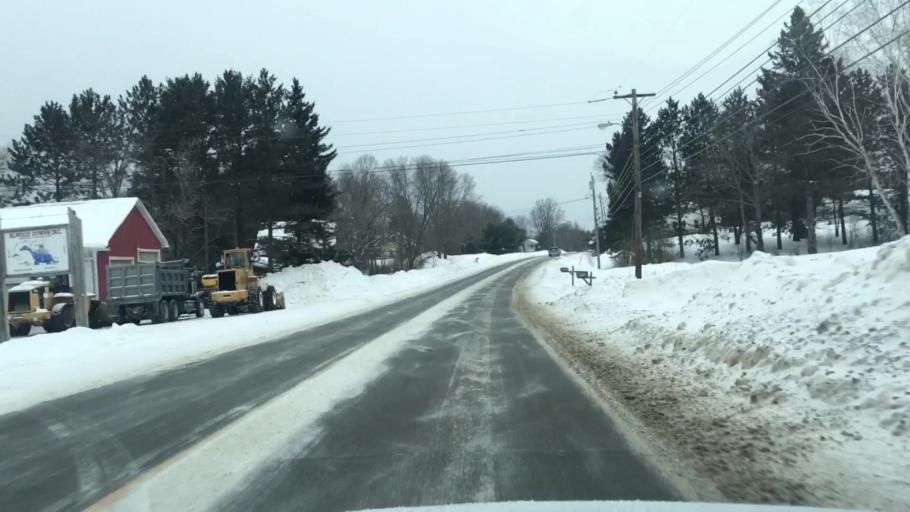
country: US
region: Maine
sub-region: Penobscot County
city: Lincoln
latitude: 45.4007
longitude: -68.4907
